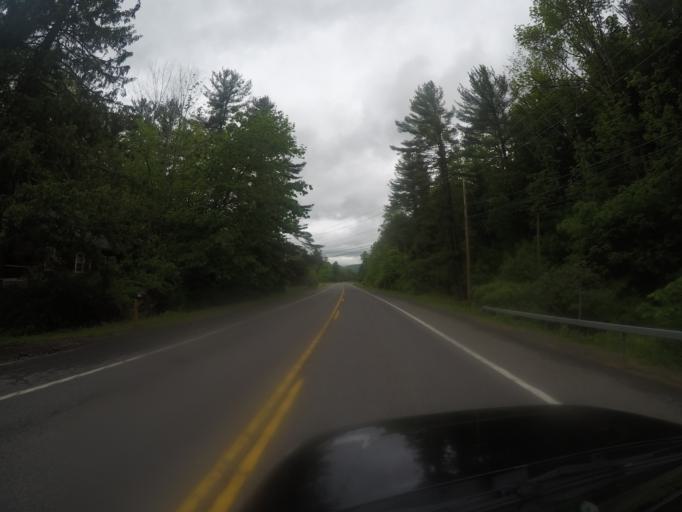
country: US
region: New York
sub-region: Ulster County
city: Shokan
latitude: 42.0936
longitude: -74.3350
